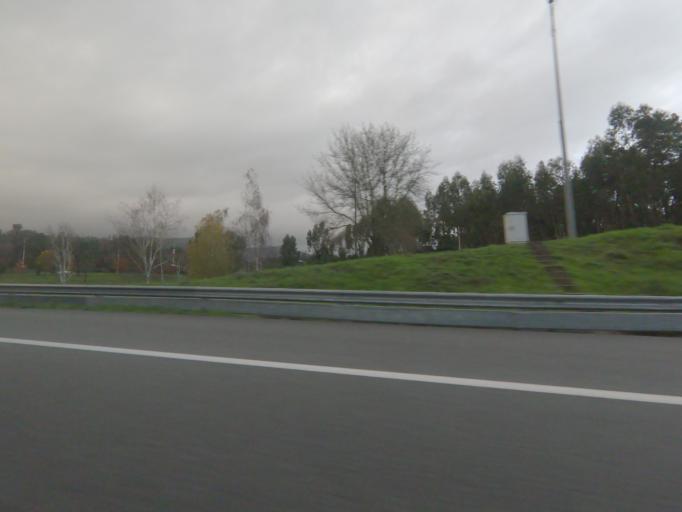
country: PT
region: Viana do Castelo
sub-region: Ponte de Lima
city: Ponte de Lima
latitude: 41.7768
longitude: -8.5597
